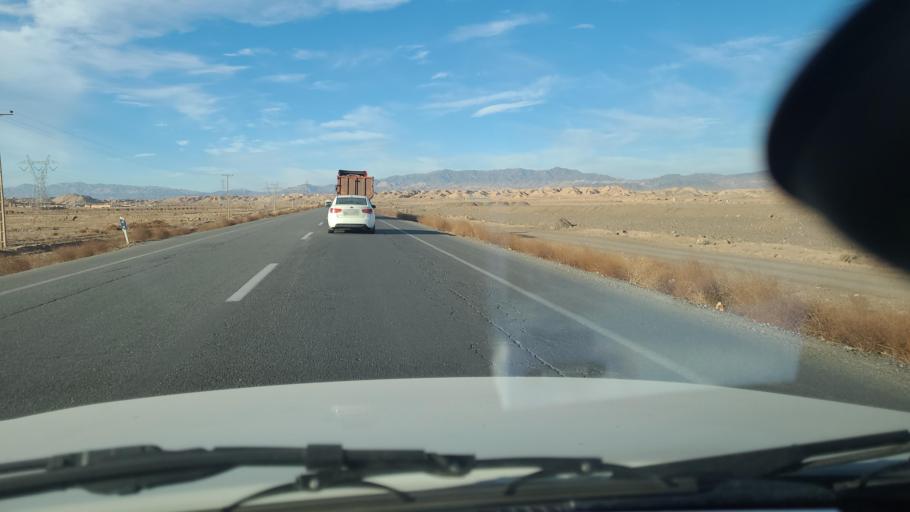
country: IR
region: Razavi Khorasan
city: Sabzevar
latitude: 36.2469
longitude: 57.6361
